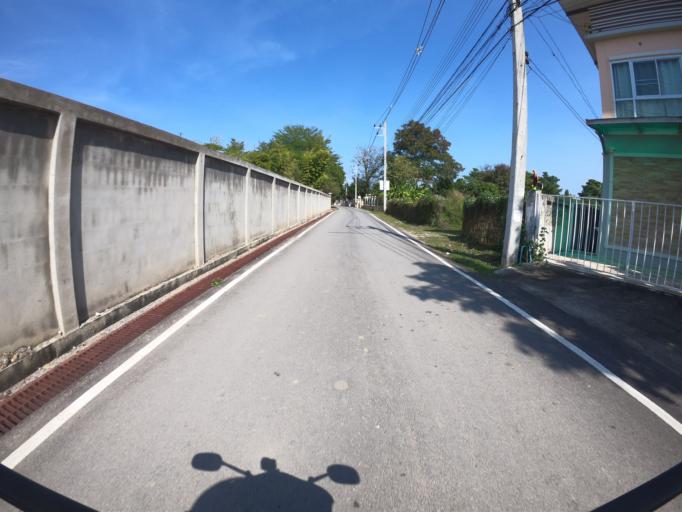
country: TH
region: Chiang Mai
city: San Sai
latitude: 18.8573
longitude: 98.9934
